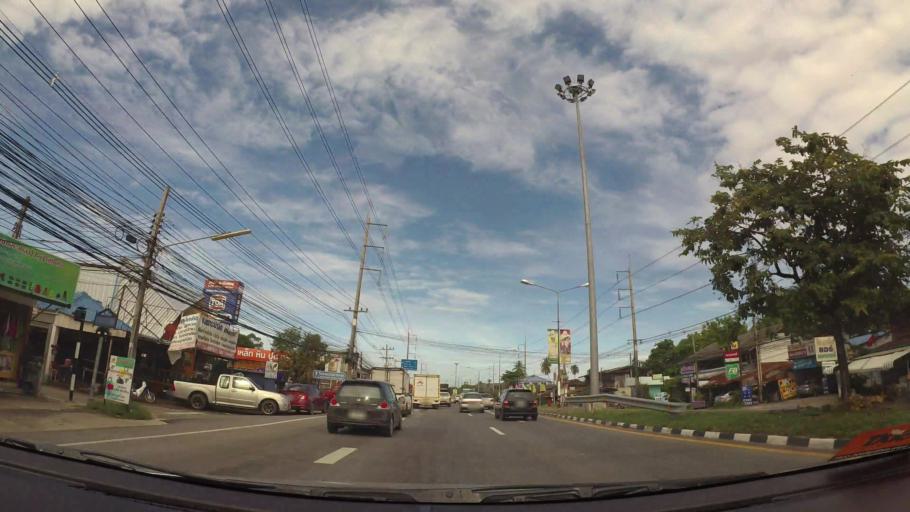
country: TH
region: Rayong
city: Ban Chang
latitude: 12.7393
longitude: 101.0847
